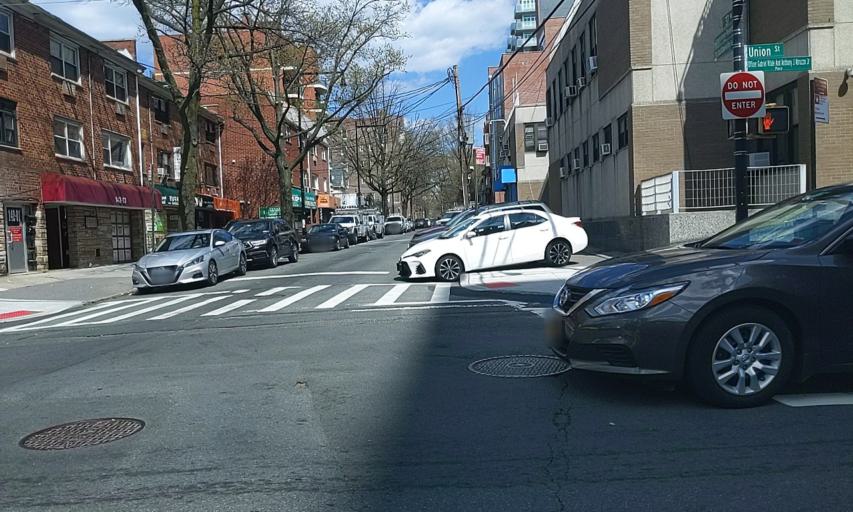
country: US
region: New York
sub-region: Queens County
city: Jamaica
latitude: 40.7624
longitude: -73.8275
